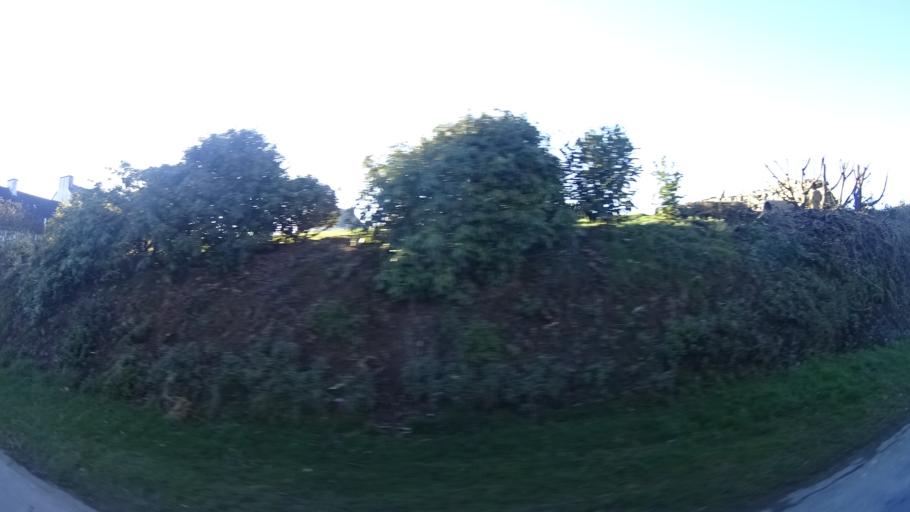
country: FR
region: Brittany
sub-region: Departement du Morbihan
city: Allaire
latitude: 47.6519
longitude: -2.1562
